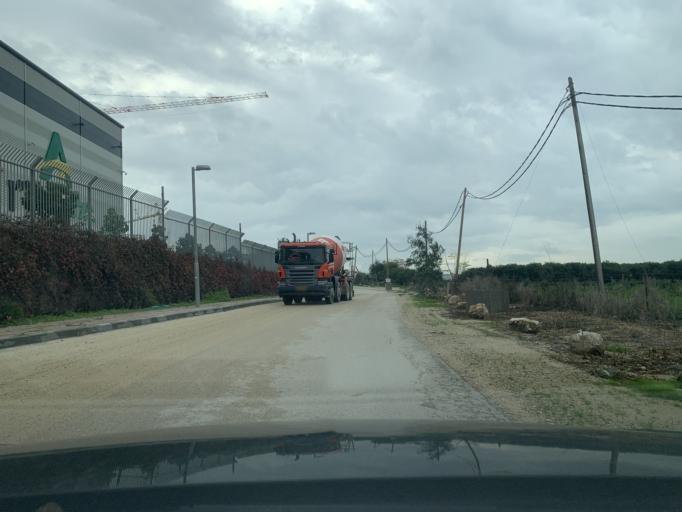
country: PS
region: West Bank
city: Qalqilyah
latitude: 32.2076
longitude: 34.9785
